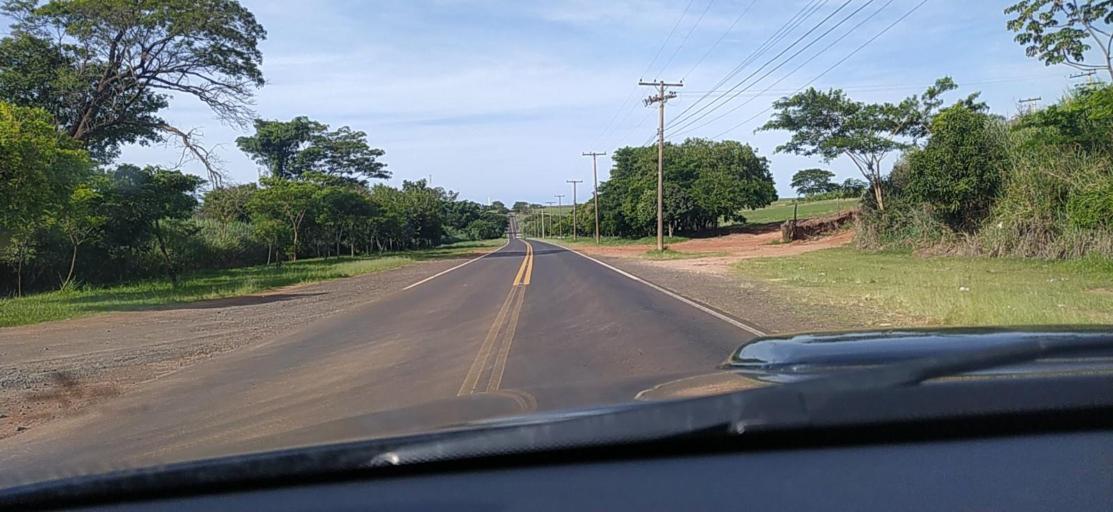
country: BR
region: Sao Paulo
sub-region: Pindorama
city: Pindorama
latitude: -21.2007
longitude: -48.9246
